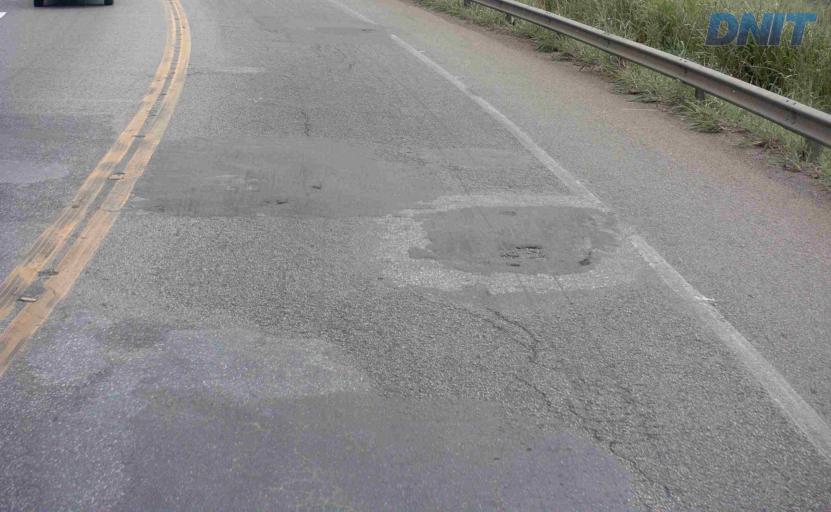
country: BR
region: Minas Gerais
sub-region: Caete
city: Caete
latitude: -19.7857
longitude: -43.7122
